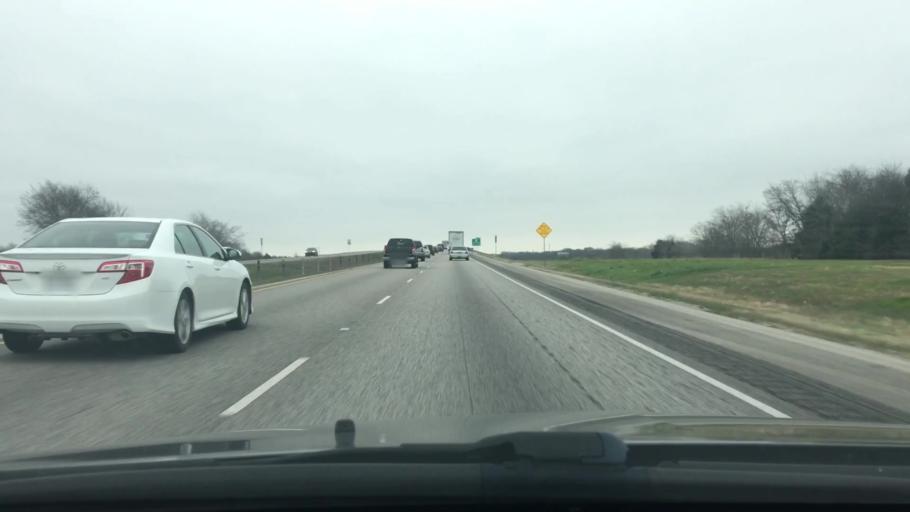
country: US
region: Texas
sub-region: Freestone County
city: Wortham
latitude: 31.8666
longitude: -96.3273
